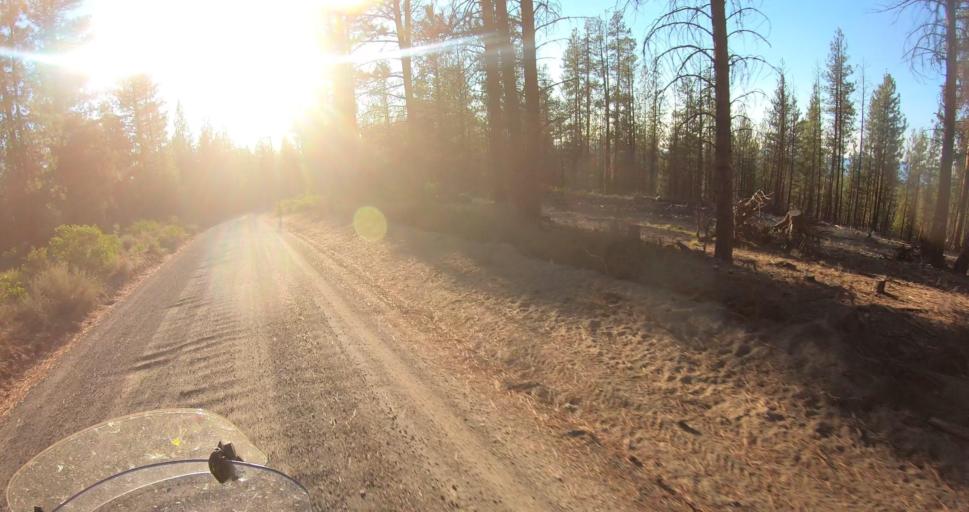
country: US
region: Oregon
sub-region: Deschutes County
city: La Pine
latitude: 43.7150
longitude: -121.3841
